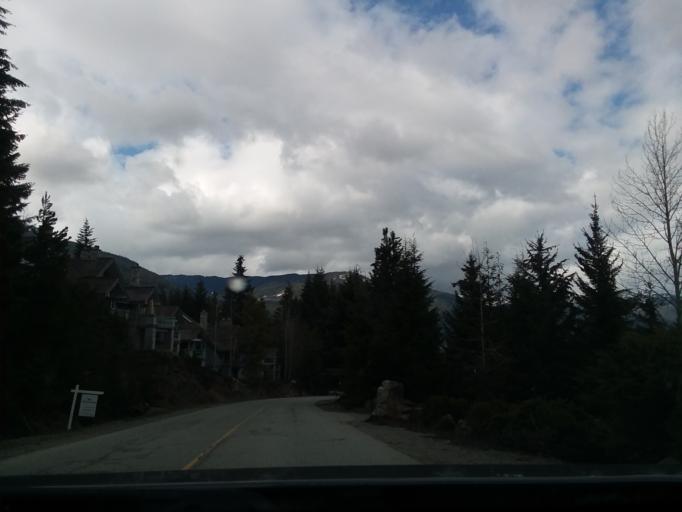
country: CA
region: British Columbia
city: Whistler
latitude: 50.1170
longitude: -122.9694
